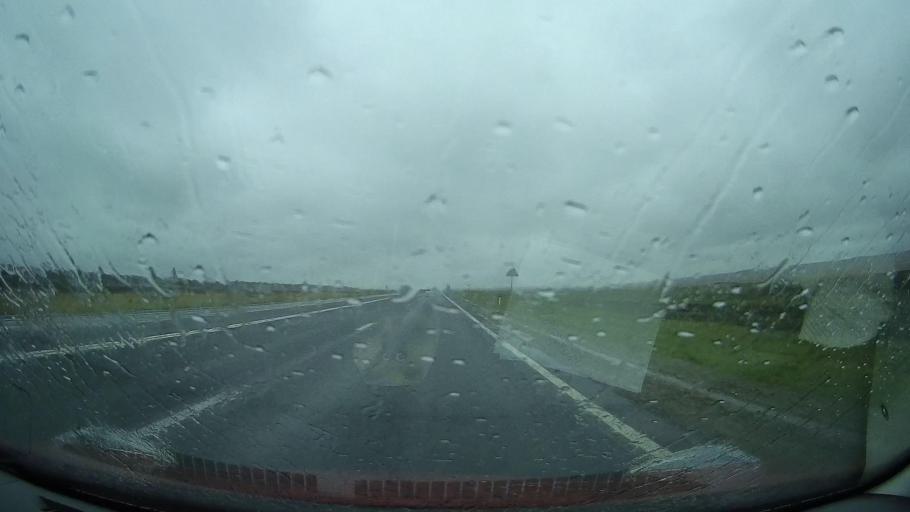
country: RU
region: Stavropol'skiy
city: Nevinnomyssk
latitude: 44.6268
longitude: 42.0508
